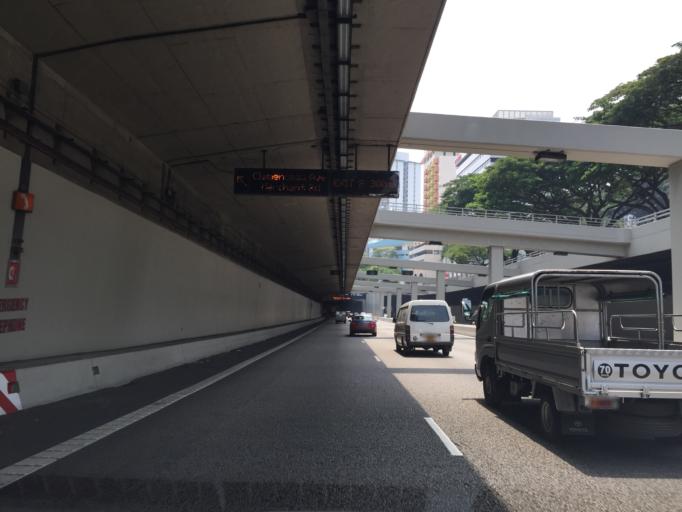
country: SG
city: Singapore
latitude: 1.2862
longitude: 103.8386
